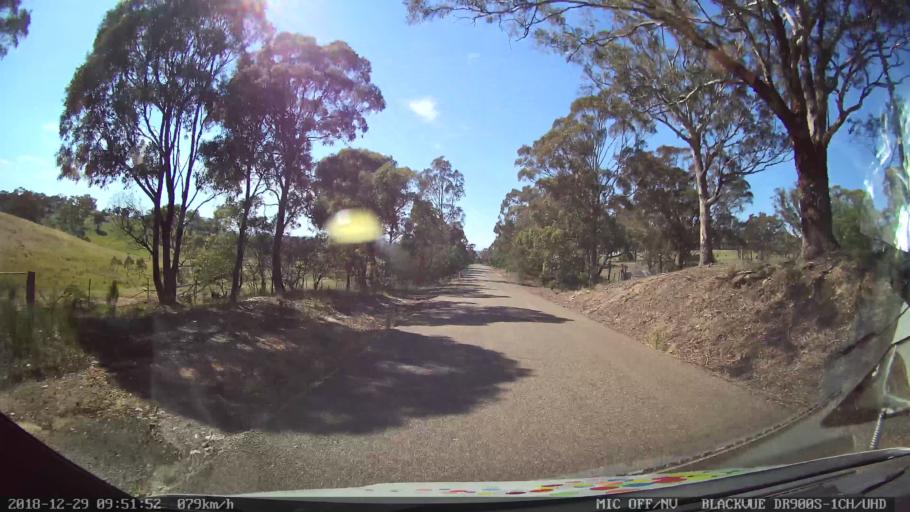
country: AU
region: New South Wales
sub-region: Goulburn Mulwaree
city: Goulburn
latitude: -34.7369
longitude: 149.4623
